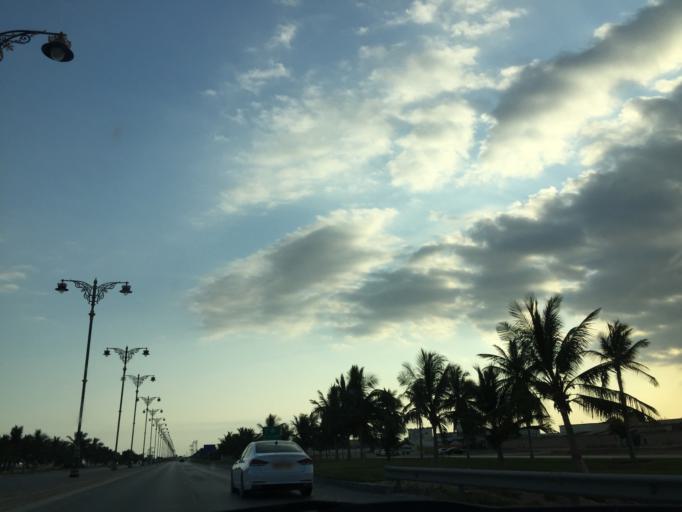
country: OM
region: Zufar
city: Salalah
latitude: 17.0434
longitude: 54.0616
